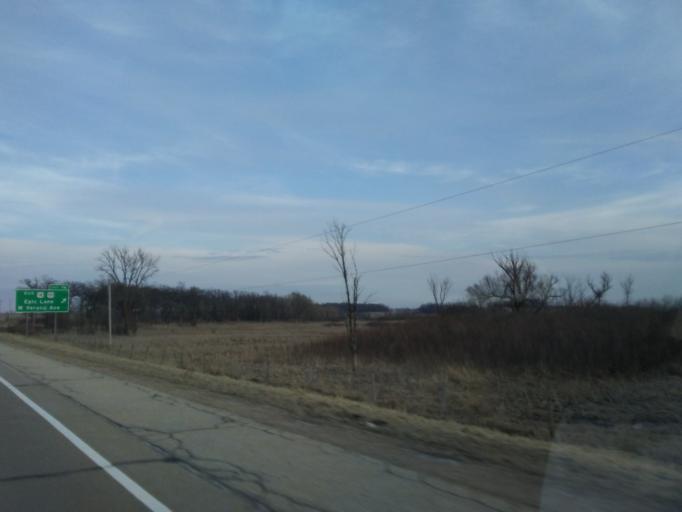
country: US
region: Wisconsin
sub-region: Dane County
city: Verona
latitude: 42.9867
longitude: -89.5703
